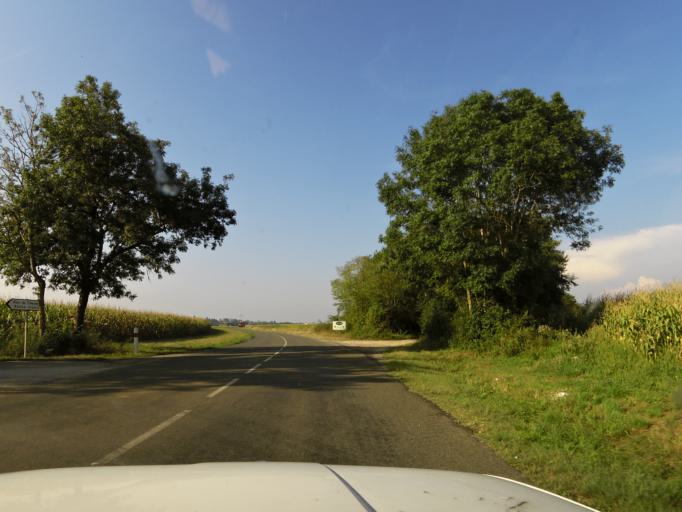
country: FR
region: Rhone-Alpes
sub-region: Departement de l'Ain
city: Chazey-sur-Ain
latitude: 45.8702
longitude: 5.2504
